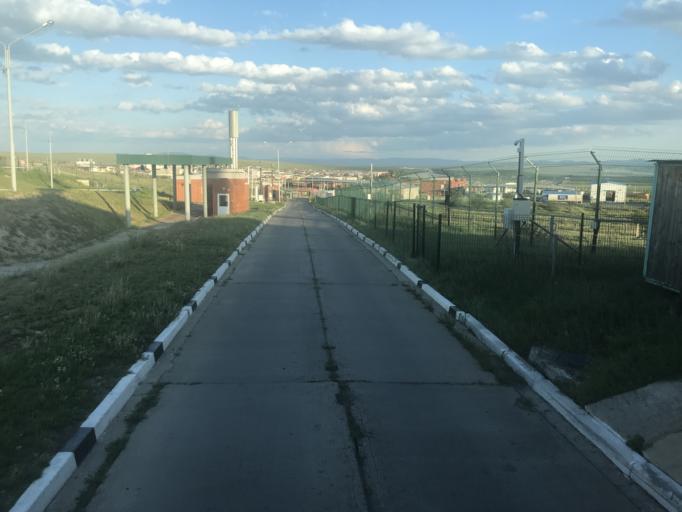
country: MN
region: Selenge
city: Altanbulag
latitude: 50.3246
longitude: 106.4880
